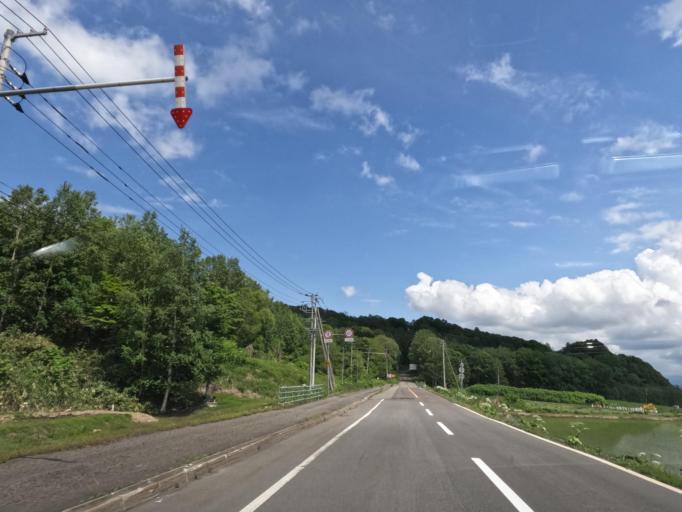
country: JP
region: Hokkaido
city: Takikawa
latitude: 43.5789
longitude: 141.8293
